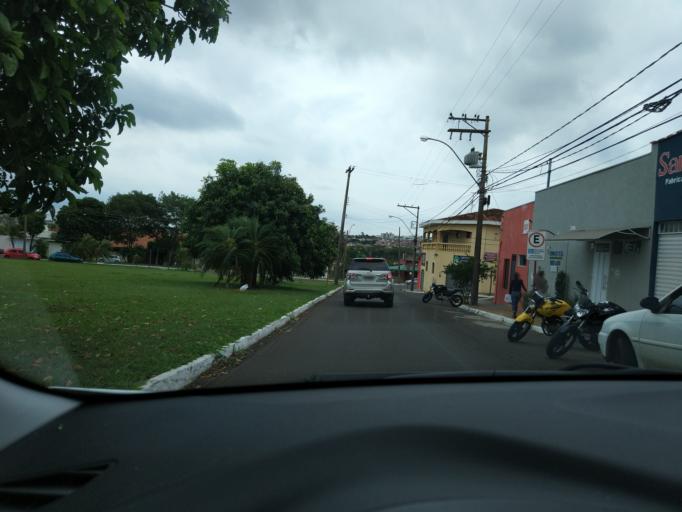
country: BR
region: Sao Paulo
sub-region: Jau
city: Jau
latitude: -22.2790
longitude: -48.5455
